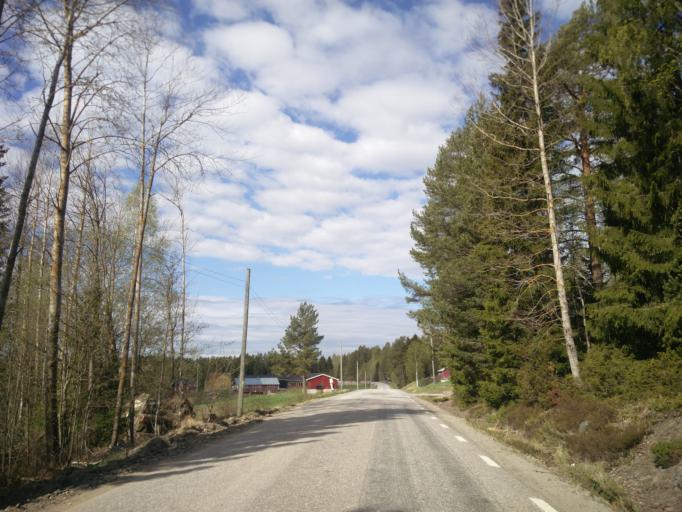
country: SE
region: Vaesternorrland
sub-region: Sundsvalls Kommun
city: Nolby
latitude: 62.2554
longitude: 17.3126
